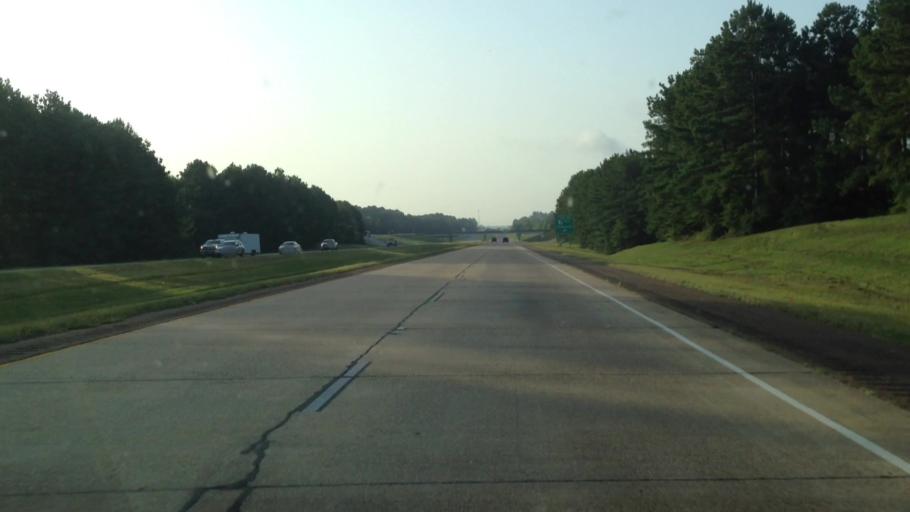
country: US
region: Louisiana
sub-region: Rapides Parish
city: Boyce
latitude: 31.4139
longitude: -92.7234
